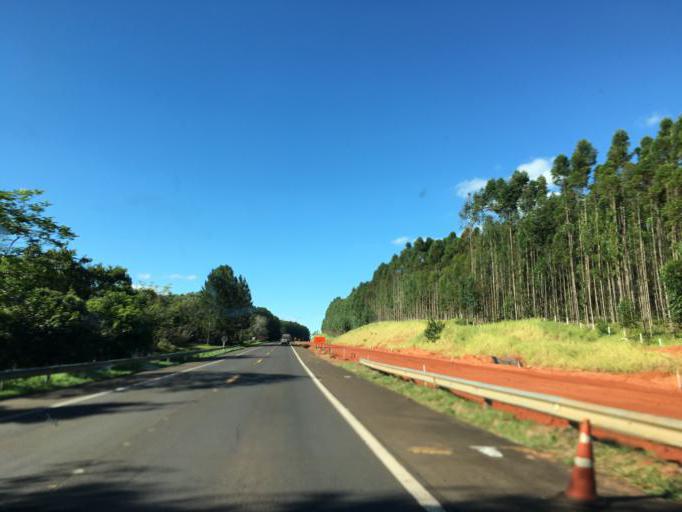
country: BR
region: Sao Paulo
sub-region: Duartina
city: Duartina
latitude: -22.5173
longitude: -49.3135
